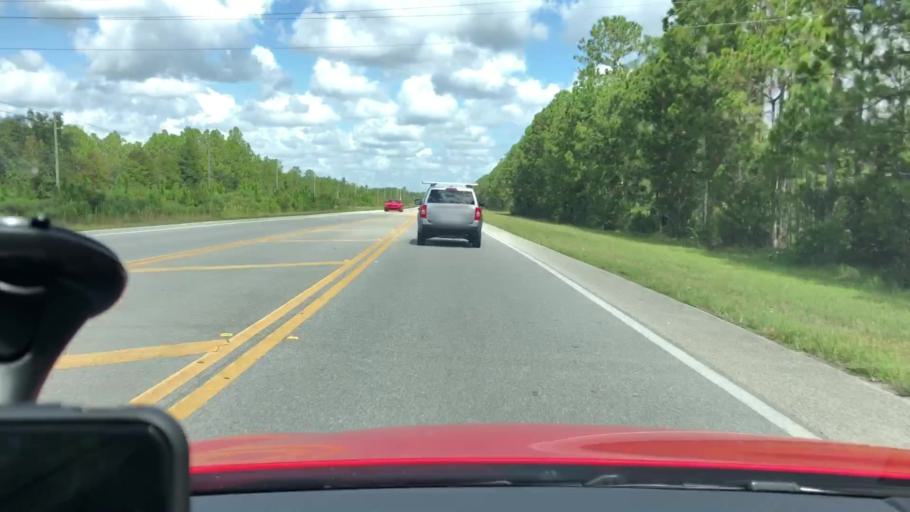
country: US
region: Florida
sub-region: Volusia County
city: Holly Hill
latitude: 29.2014
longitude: -81.1198
